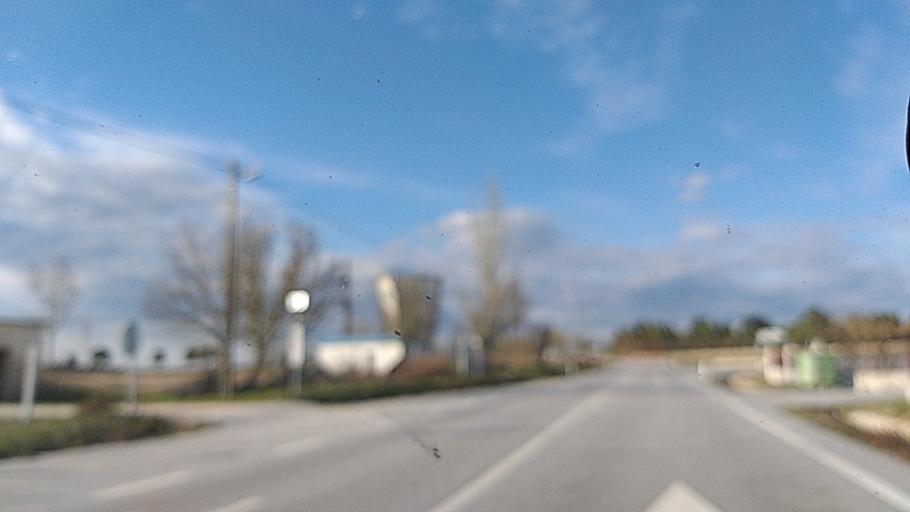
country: ES
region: Castille and Leon
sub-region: Provincia de Salamanca
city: Aldea del Obispo
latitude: 40.6602
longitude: -6.8570
